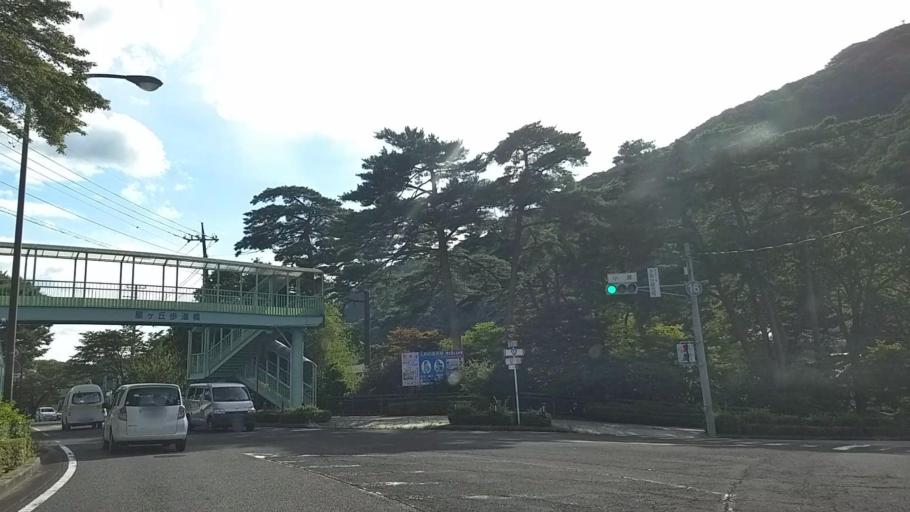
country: JP
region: Tochigi
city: Imaichi
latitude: 36.8424
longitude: 139.7228
